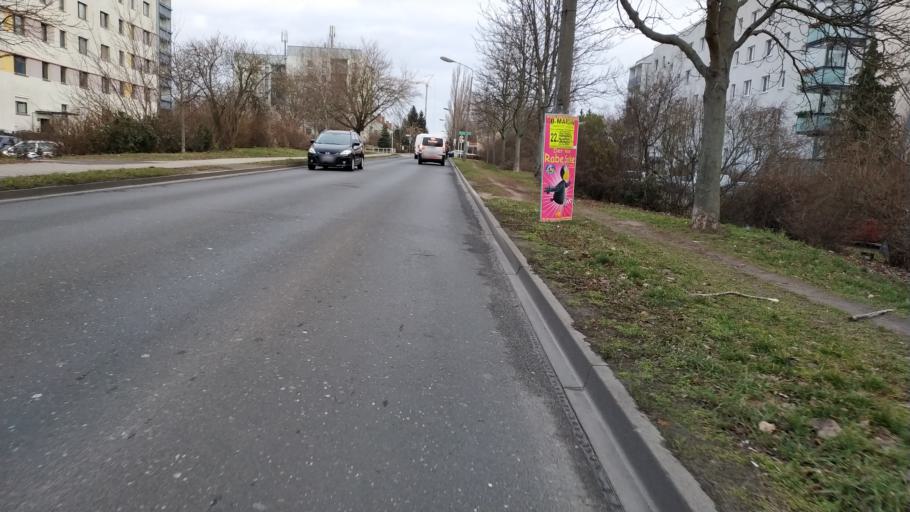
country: DE
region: Berlin
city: Hellersdorf
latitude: 52.5360
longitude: 13.5917
